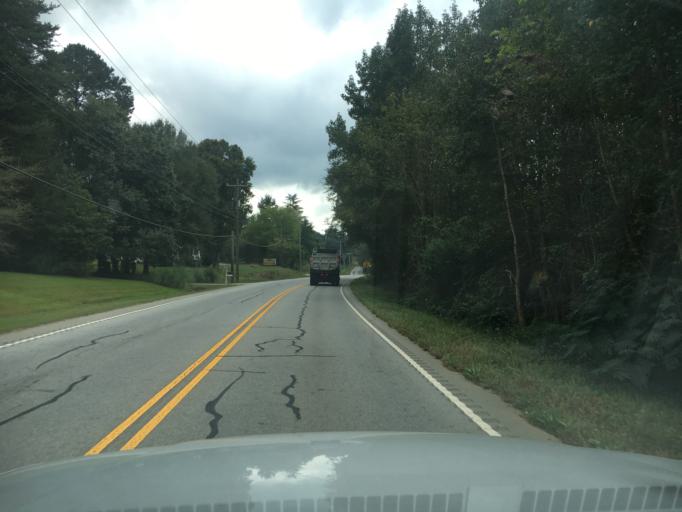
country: US
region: South Carolina
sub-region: Greenville County
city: Greer
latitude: 34.9616
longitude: -82.2325
